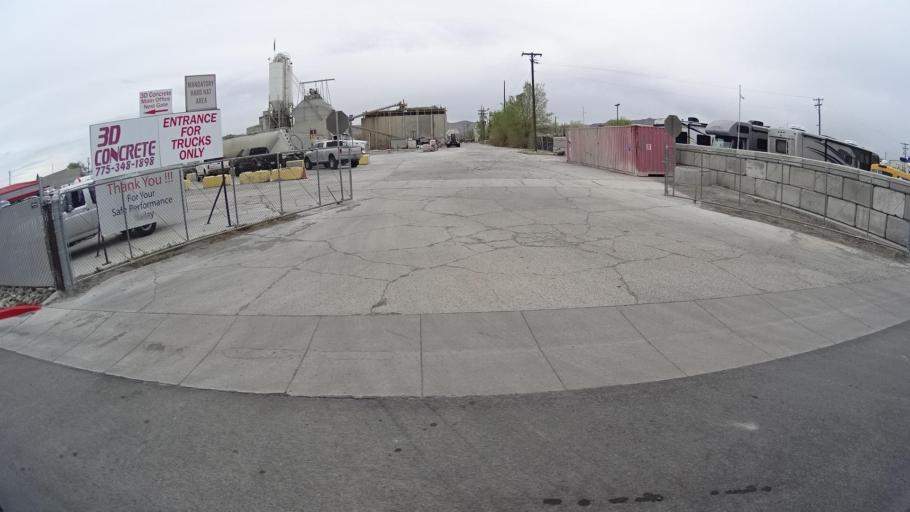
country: US
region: Nevada
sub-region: Washoe County
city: Sparks
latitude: 39.5291
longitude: -119.7714
